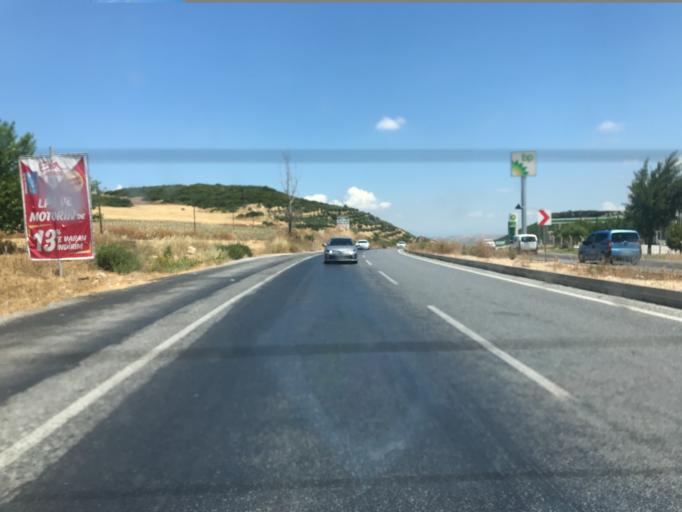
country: TR
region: Aydin
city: Akkoy
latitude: 37.4833
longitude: 27.3386
